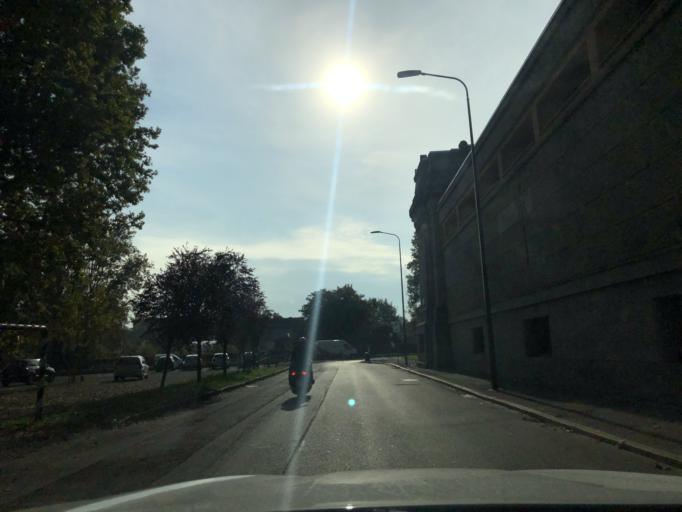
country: IT
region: Lombardy
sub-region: Citta metropolitana di Milano
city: Baranzate
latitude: 45.5024
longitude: 9.1192
